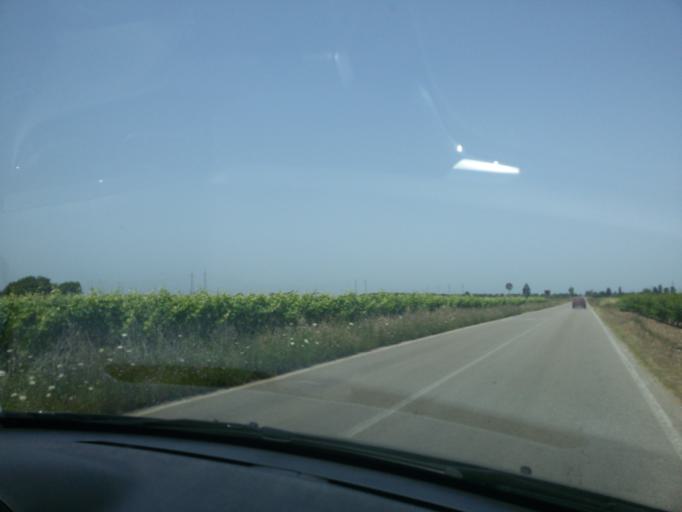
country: IT
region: Apulia
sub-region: Provincia di Brindisi
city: San Pancrazio Salentino
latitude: 40.3859
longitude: 17.8362
